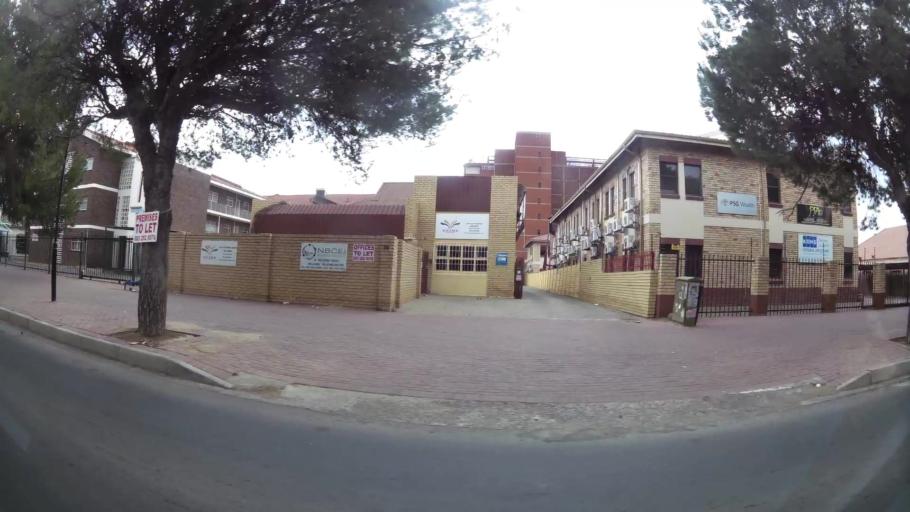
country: ZA
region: Orange Free State
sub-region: Mangaung Metropolitan Municipality
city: Bloemfontein
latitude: -29.1218
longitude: 26.2017
